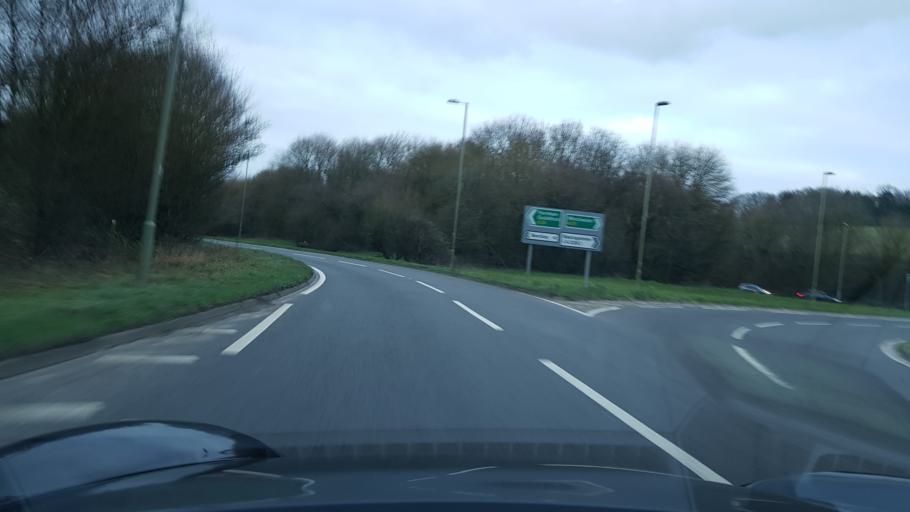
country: GB
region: England
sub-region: Hampshire
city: Alton
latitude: 51.1574
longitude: -0.9508
